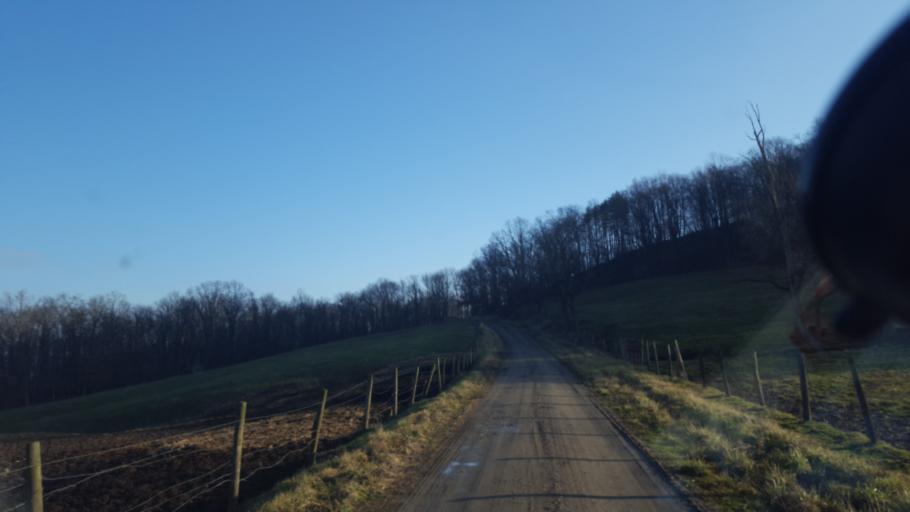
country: US
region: Ohio
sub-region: Guernsey County
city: Byesville
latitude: 40.0922
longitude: -81.3755
